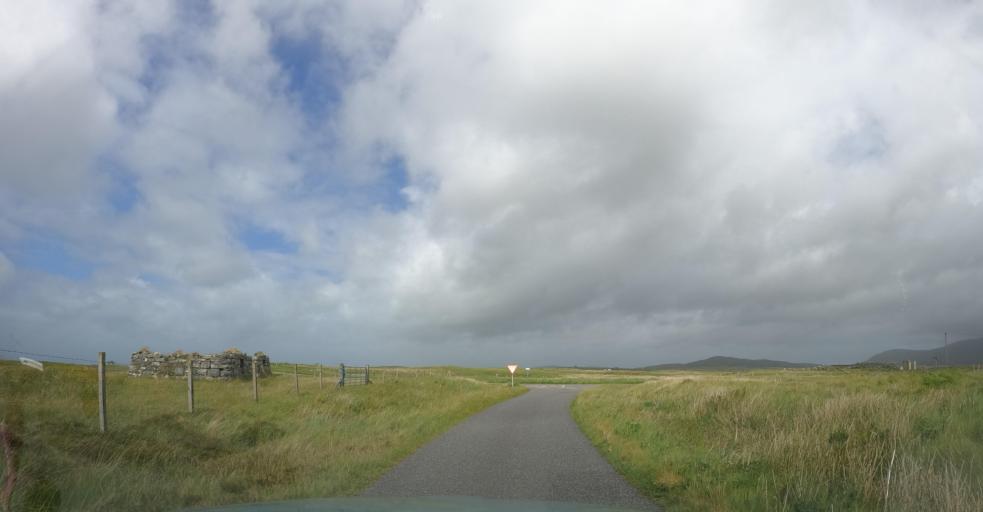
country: GB
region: Scotland
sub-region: Eilean Siar
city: Isle of South Uist
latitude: 57.2714
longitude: -7.3992
